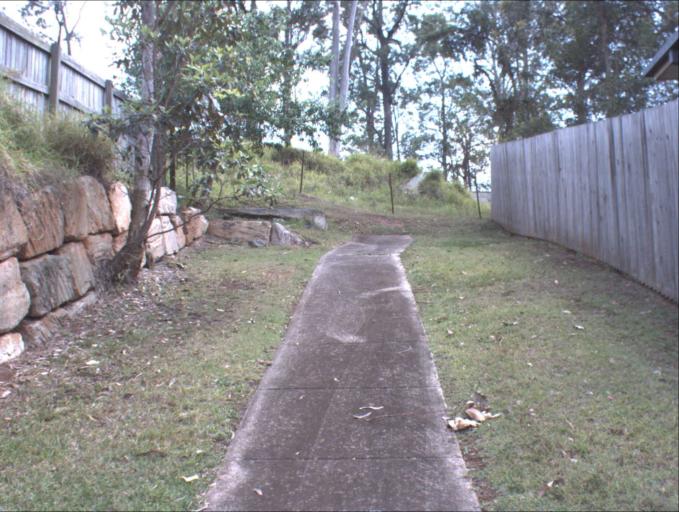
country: AU
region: Queensland
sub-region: Logan
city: Woodridge
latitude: -27.6143
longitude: 153.1031
